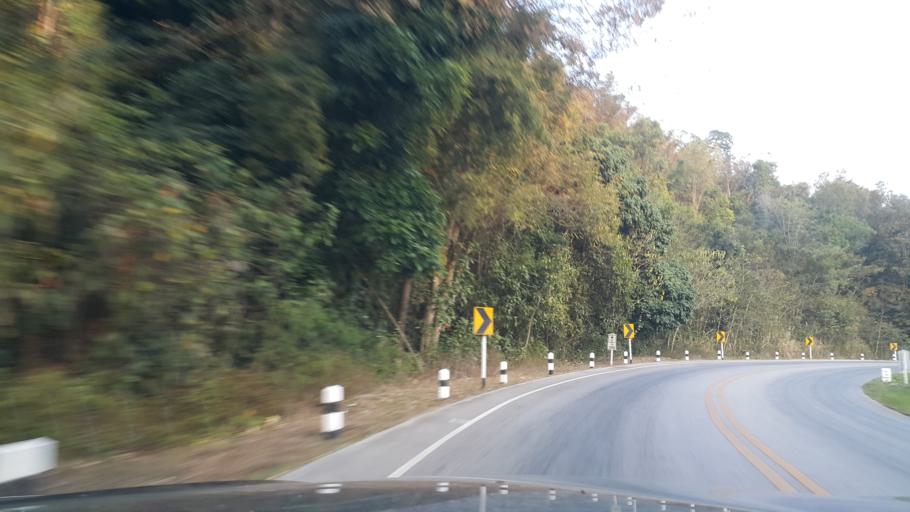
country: TH
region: Loei
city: Loei
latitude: 17.4702
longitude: 101.5856
